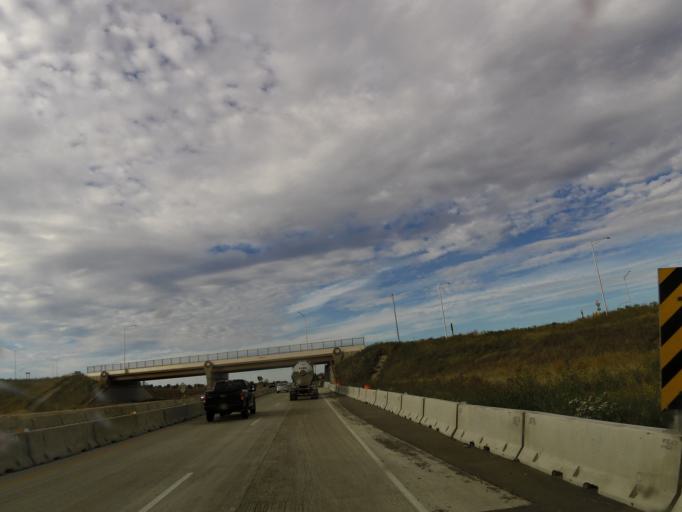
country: US
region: Wisconsin
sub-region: Rock County
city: Edgerton
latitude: 42.8348
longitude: -89.0277
